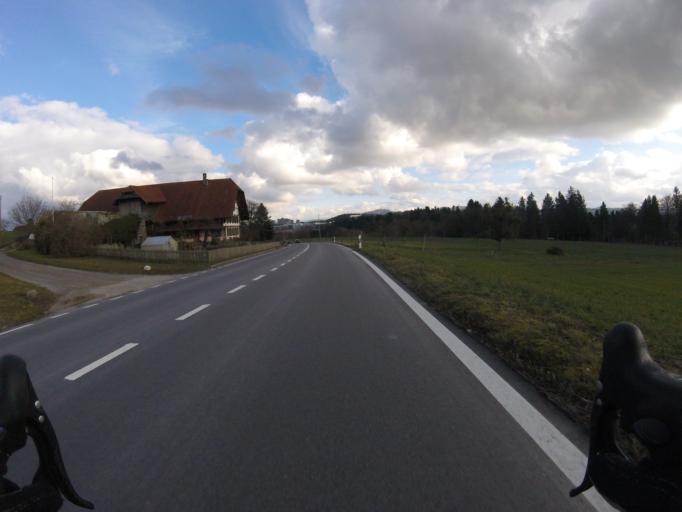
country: CH
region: Bern
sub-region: Bern-Mittelland District
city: Wohlen
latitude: 46.9480
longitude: 7.3615
